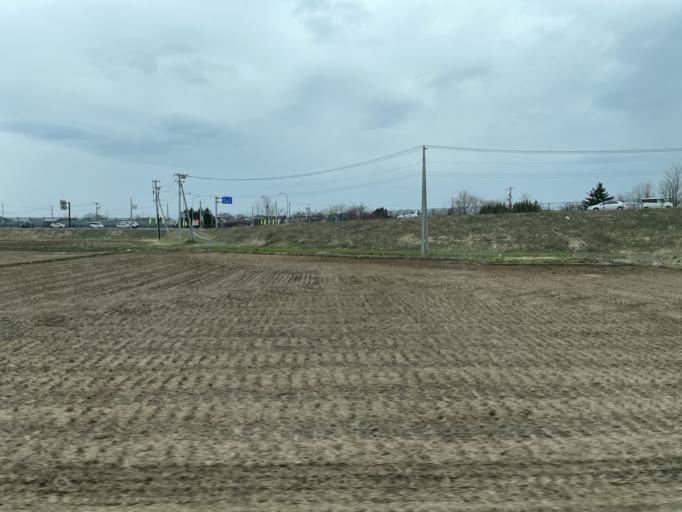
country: JP
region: Aomori
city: Namioka
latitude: 40.7035
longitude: 140.5743
